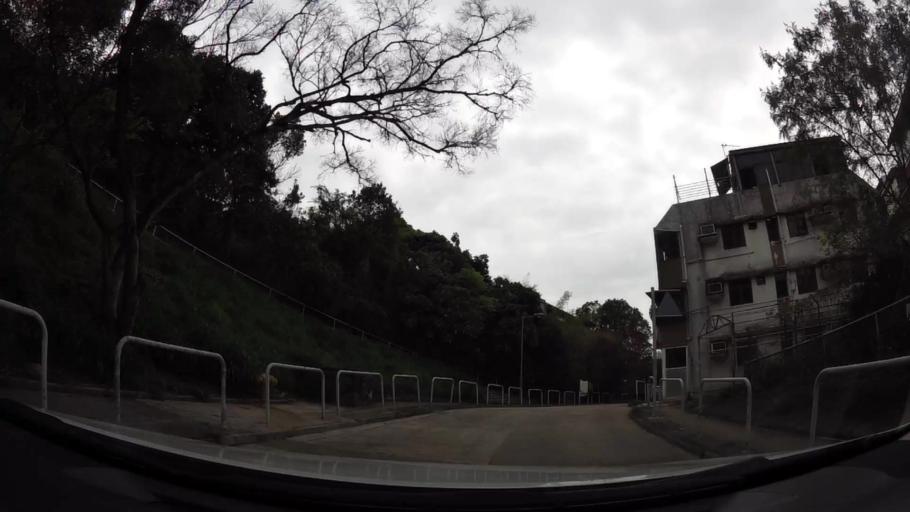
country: HK
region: Tuen Mun
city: Tuen Mun
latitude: 22.4013
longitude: 113.9801
